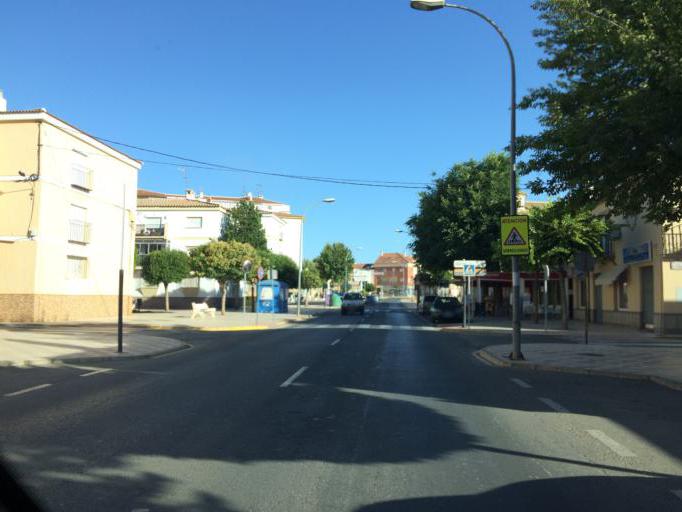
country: ES
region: Andalusia
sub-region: Provincia de Malaga
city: Campillos
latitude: 37.0452
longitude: -4.8643
